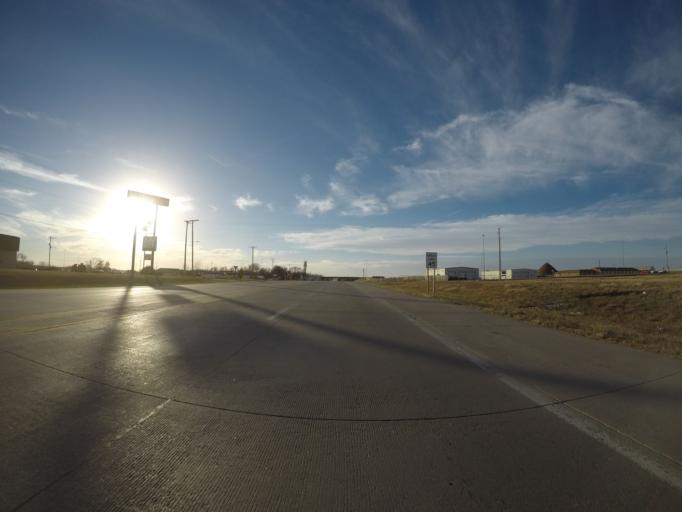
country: US
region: Kansas
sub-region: Lyon County
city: Emporia
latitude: 38.4123
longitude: -96.2345
